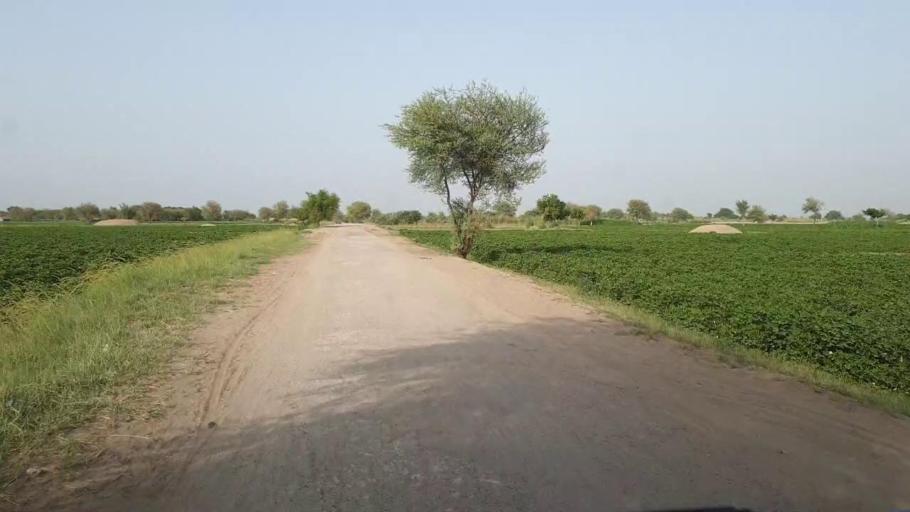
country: PK
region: Sindh
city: Daur
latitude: 26.3410
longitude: 68.2583
